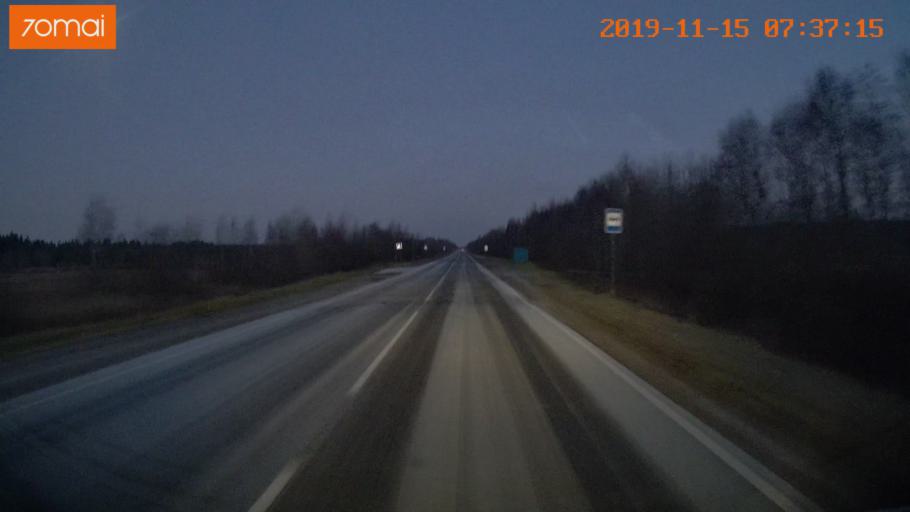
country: RU
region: Vologda
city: Sheksna
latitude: 58.7481
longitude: 38.4205
